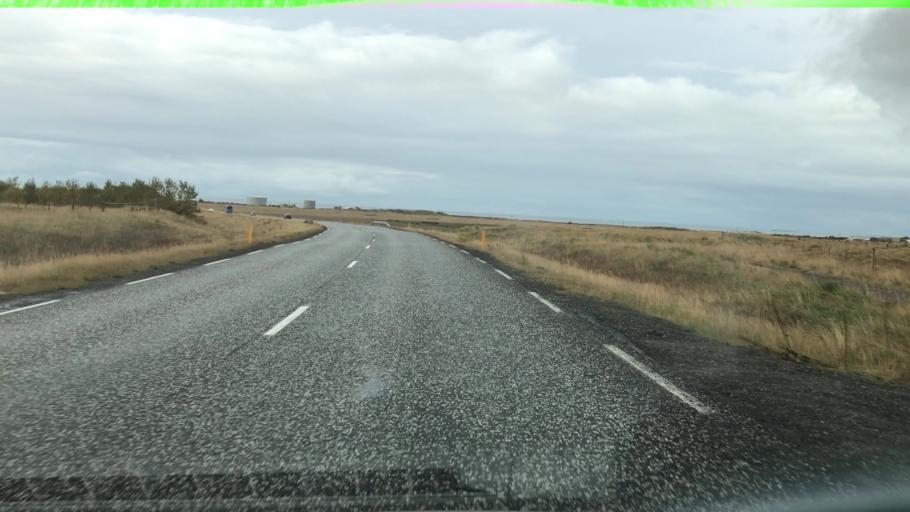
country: IS
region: West
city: Akranes
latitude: 64.3244
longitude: -22.0159
